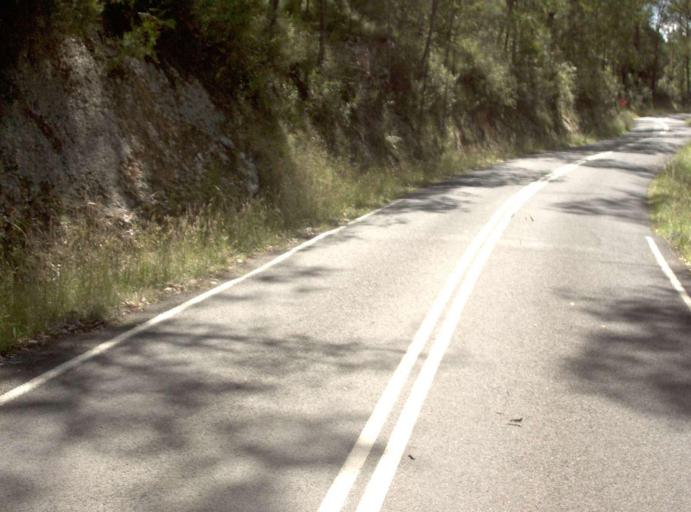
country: AU
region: Victoria
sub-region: Baw Baw
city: Warragul
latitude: -37.9074
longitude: 146.0199
